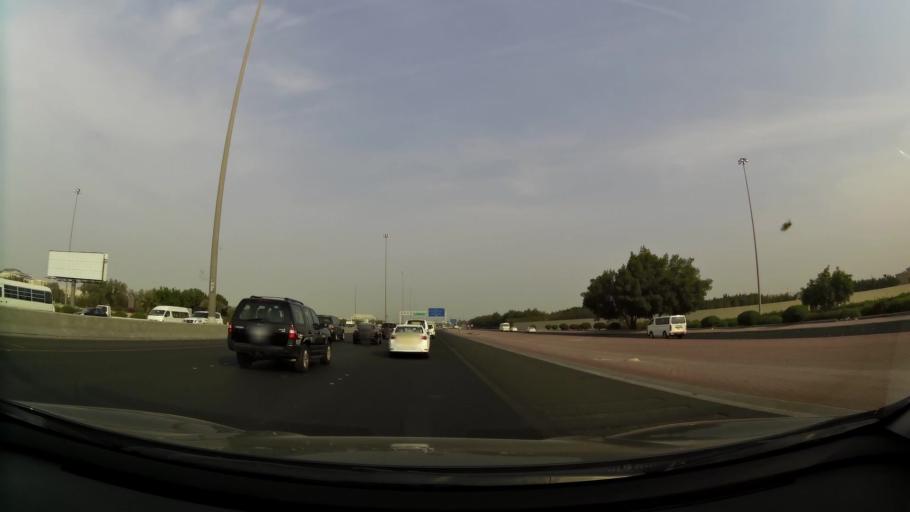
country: KW
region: Al Farwaniyah
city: Janub as Surrah
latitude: 29.2644
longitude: 48.0140
